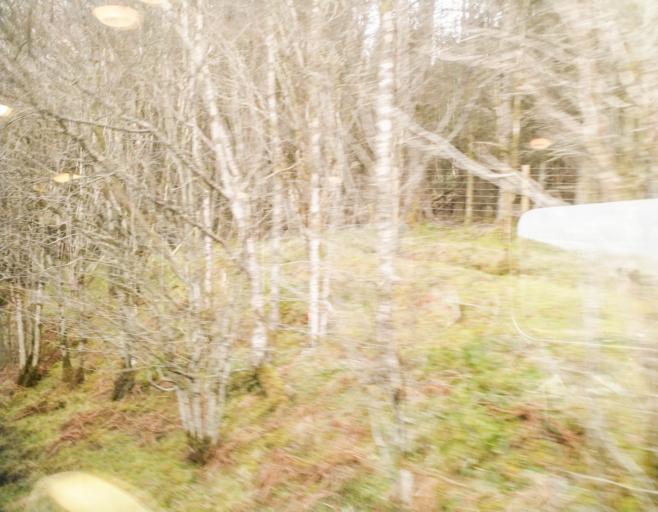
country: GB
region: Scotland
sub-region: Argyll and Bute
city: Garelochhead
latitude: 56.4416
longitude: -4.7076
